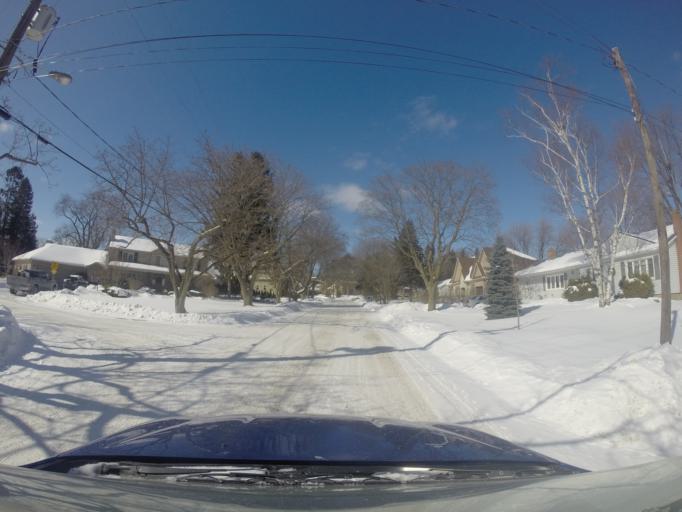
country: CA
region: Ontario
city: Burlington
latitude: 43.3407
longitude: -79.7695
